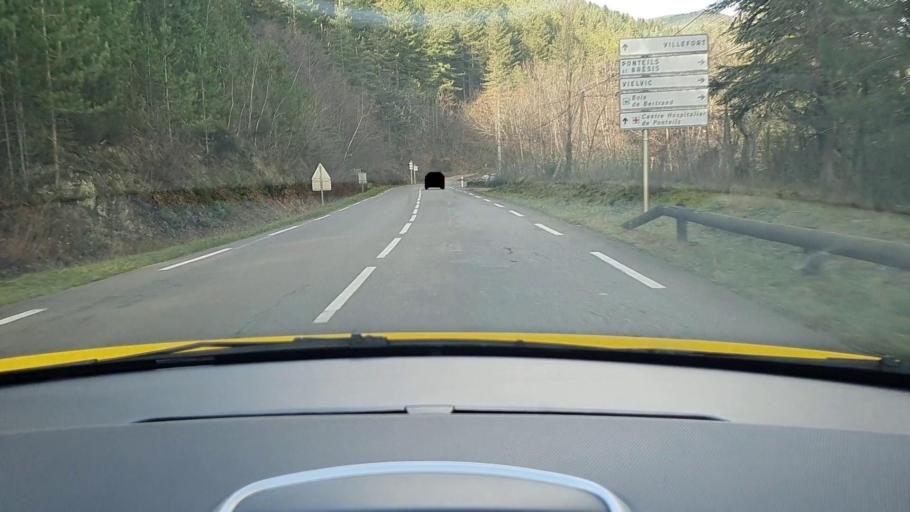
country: FR
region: Languedoc-Roussillon
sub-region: Departement du Gard
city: Branoux-les-Taillades
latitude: 44.3880
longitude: 3.9376
